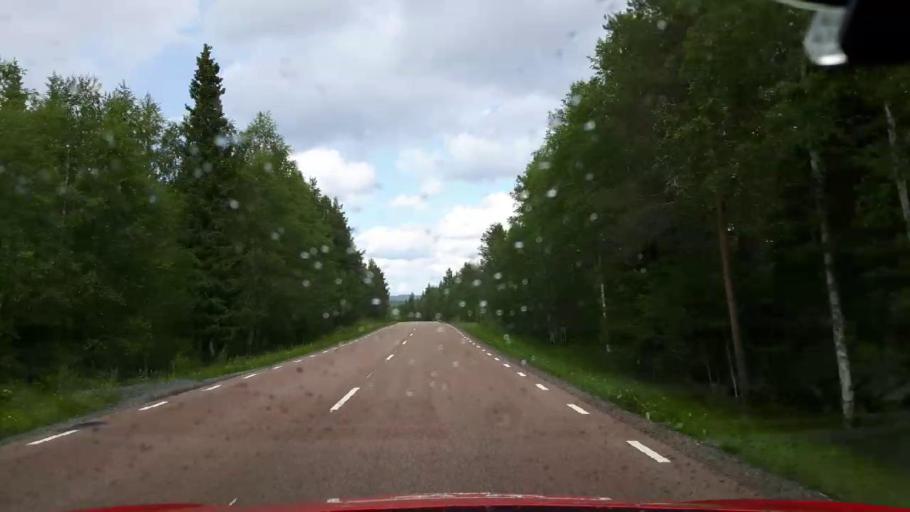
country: SE
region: Jaemtland
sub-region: Krokoms Kommun
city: Valla
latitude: 63.9403
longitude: 14.2228
